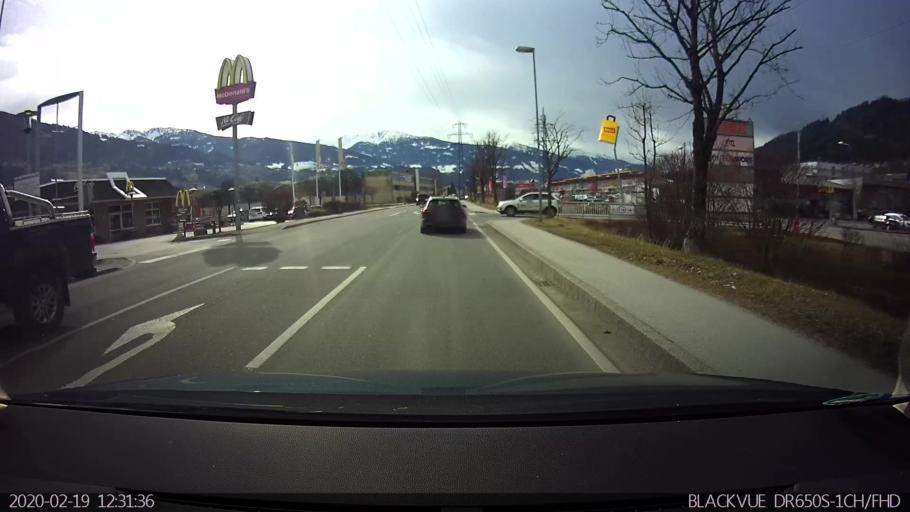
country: AT
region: Tyrol
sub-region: Politischer Bezirk Schwaz
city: Schwaz
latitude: 47.3509
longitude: 11.6987
